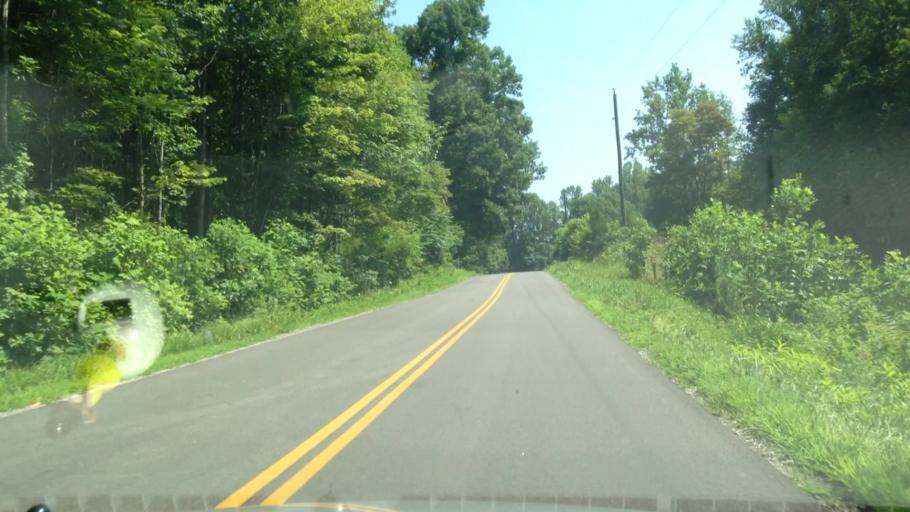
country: US
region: Virginia
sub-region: Patrick County
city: Patrick Springs
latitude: 36.5797
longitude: -80.1920
